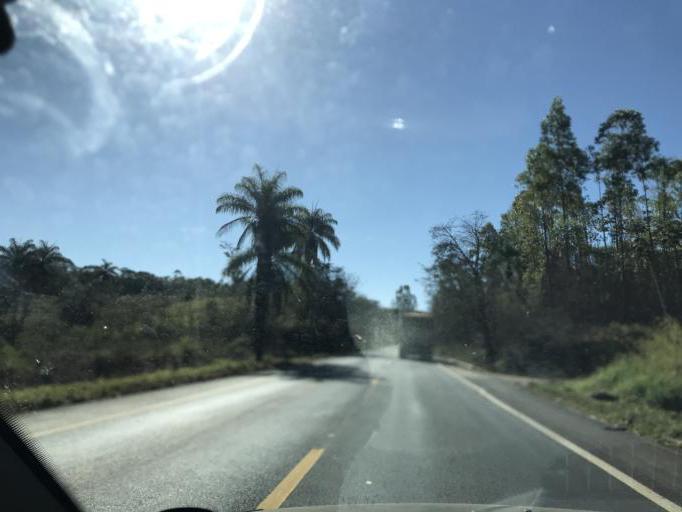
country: BR
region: Minas Gerais
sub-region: Bambui
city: Bambui
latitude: -19.8731
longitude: -45.9856
